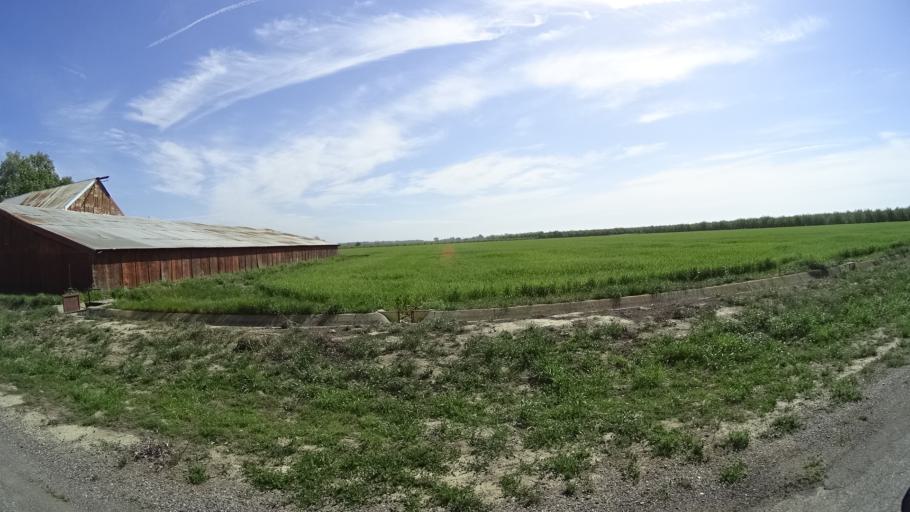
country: US
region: California
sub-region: Glenn County
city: Hamilton City
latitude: 39.6213
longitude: -122.0182
